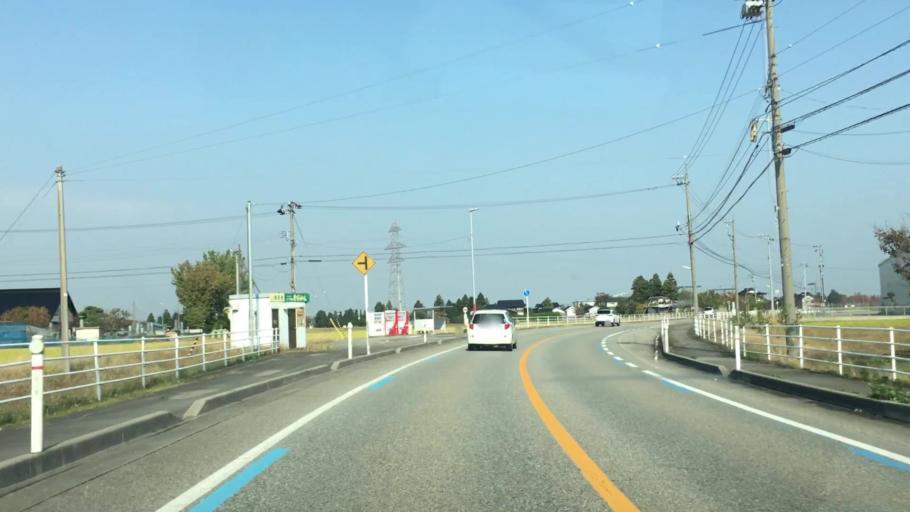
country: JP
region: Toyama
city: Yatsuomachi-higashikumisaka
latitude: 36.6161
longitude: 137.1918
